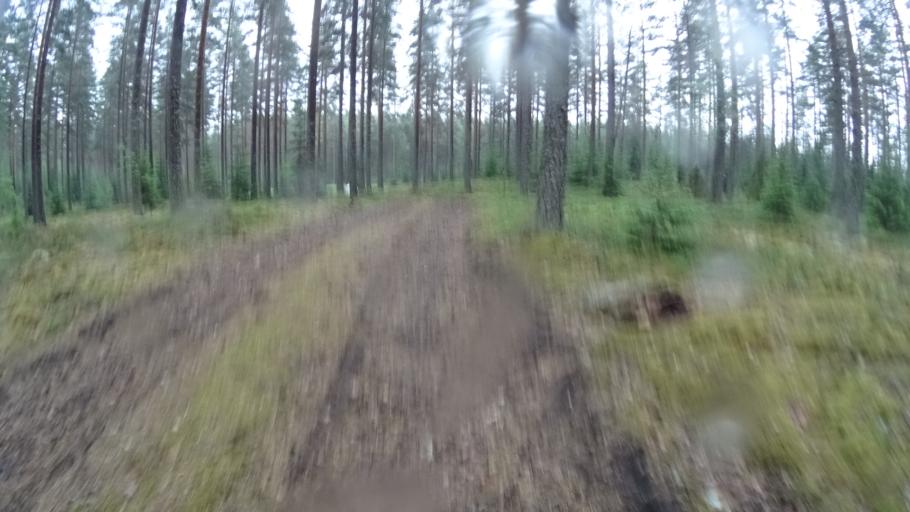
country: FI
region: Uusimaa
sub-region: Helsinki
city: Karkkila
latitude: 60.5913
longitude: 24.1852
